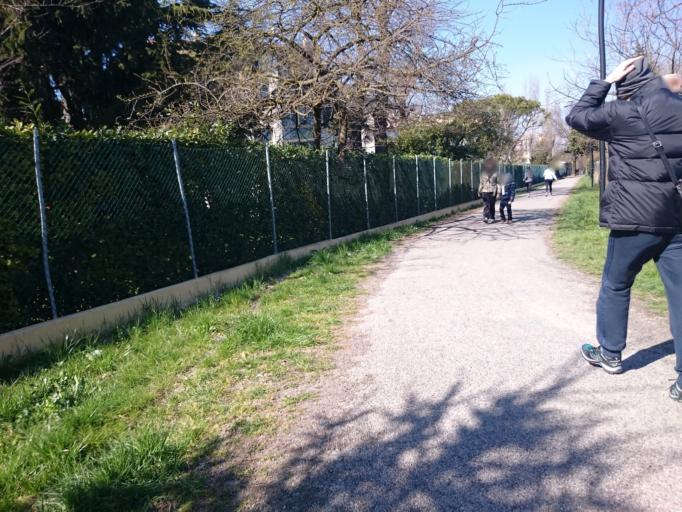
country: IT
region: Veneto
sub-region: Provincia di Padova
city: Padova
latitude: 45.3896
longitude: 11.8977
